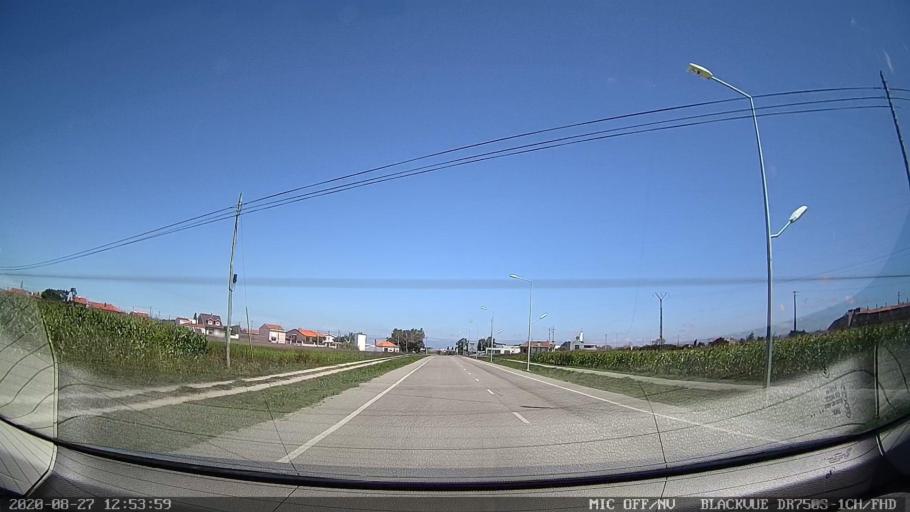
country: PT
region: Aveiro
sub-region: Ilhavo
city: Ilhavo
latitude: 40.5973
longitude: -8.6786
